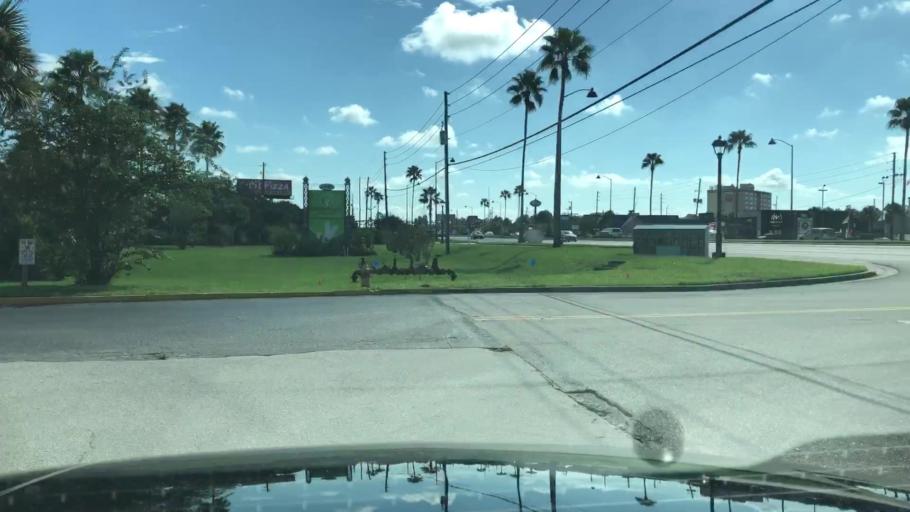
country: US
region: Florida
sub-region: Osceola County
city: Celebration
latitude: 28.3332
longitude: -81.4937
